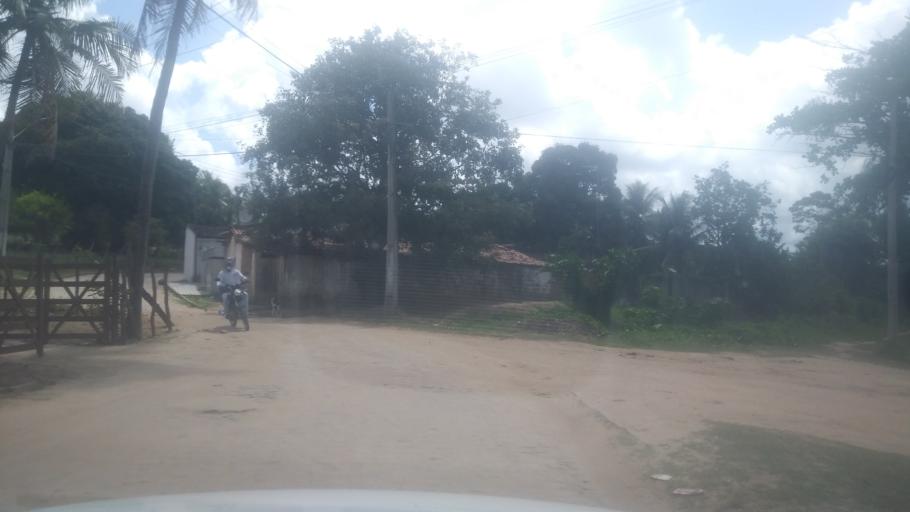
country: BR
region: Rio Grande do Norte
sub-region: Sao Jose De Mipibu
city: Sao Jose de Mipibu
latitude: -6.0716
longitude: -35.2325
